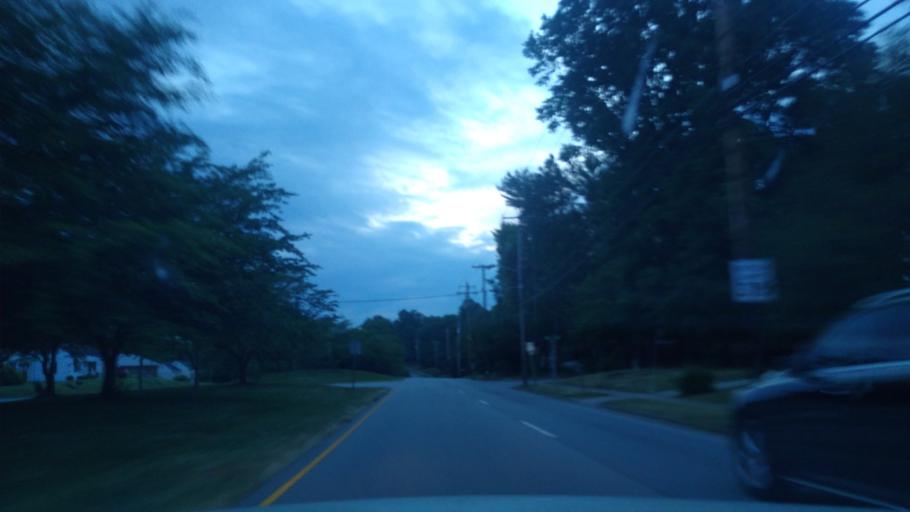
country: US
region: North Carolina
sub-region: Guilford County
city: Greensboro
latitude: 36.1136
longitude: -79.7694
